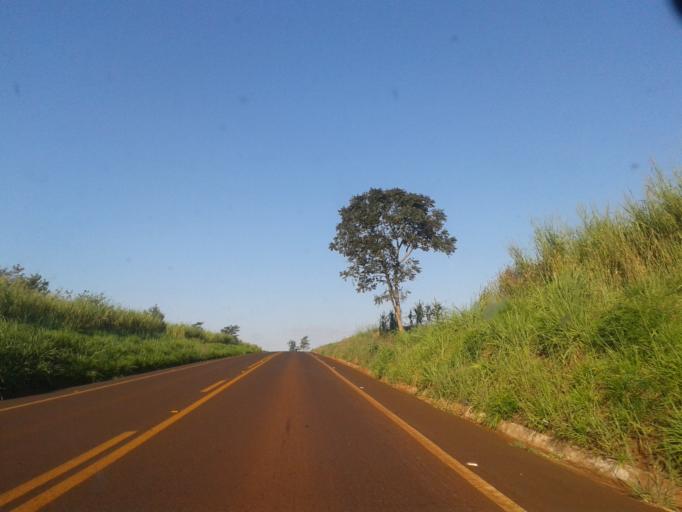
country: BR
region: Minas Gerais
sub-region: Capinopolis
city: Capinopolis
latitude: -18.7119
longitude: -49.7329
